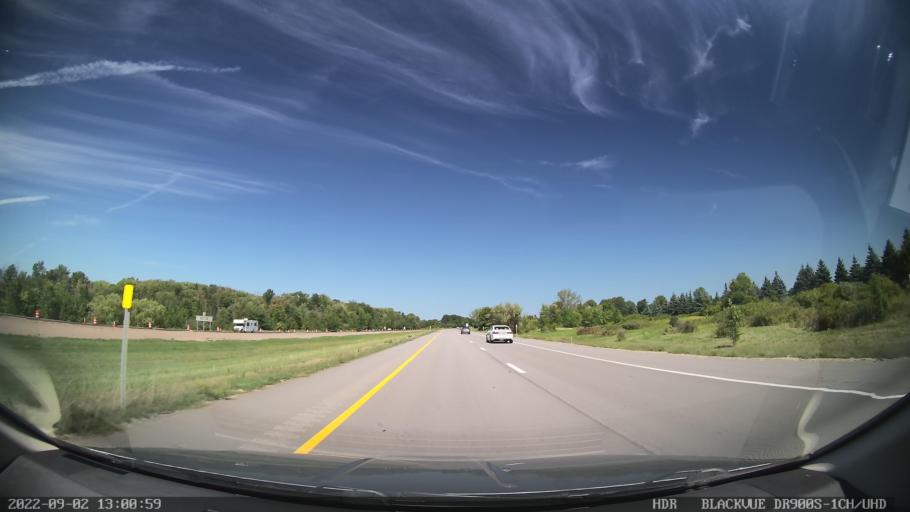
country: US
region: New York
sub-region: Monroe County
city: Scottsville
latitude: 43.0286
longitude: -77.6553
